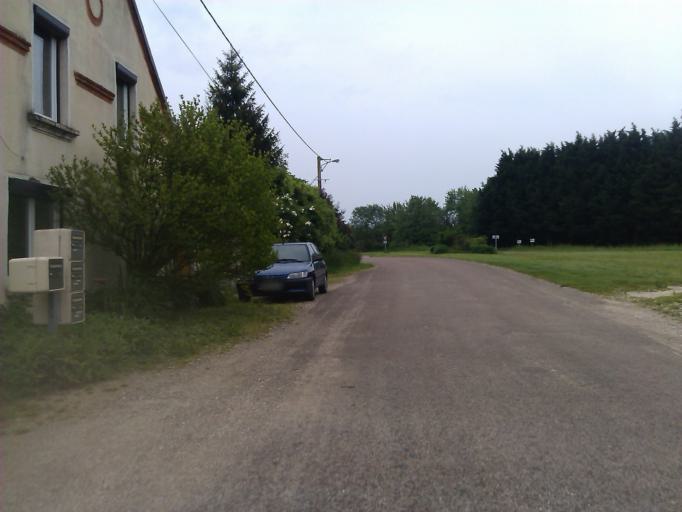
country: FR
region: Bourgogne
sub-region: Departement de la Cote-d'Or
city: Seurre
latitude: 47.0532
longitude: 5.1885
